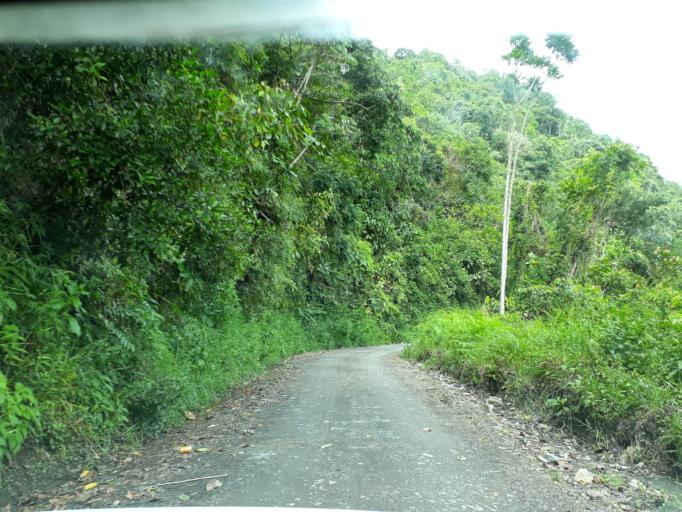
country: CO
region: Boyaca
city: Quipama
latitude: 5.4338
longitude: -74.1852
